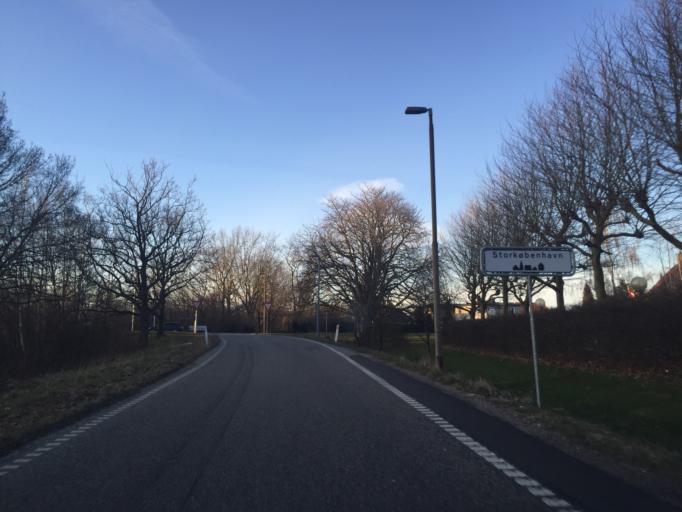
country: DK
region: Capital Region
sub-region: Lyngby-Tarbaek Kommune
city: Kongens Lyngby
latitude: 55.7819
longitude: 12.4860
